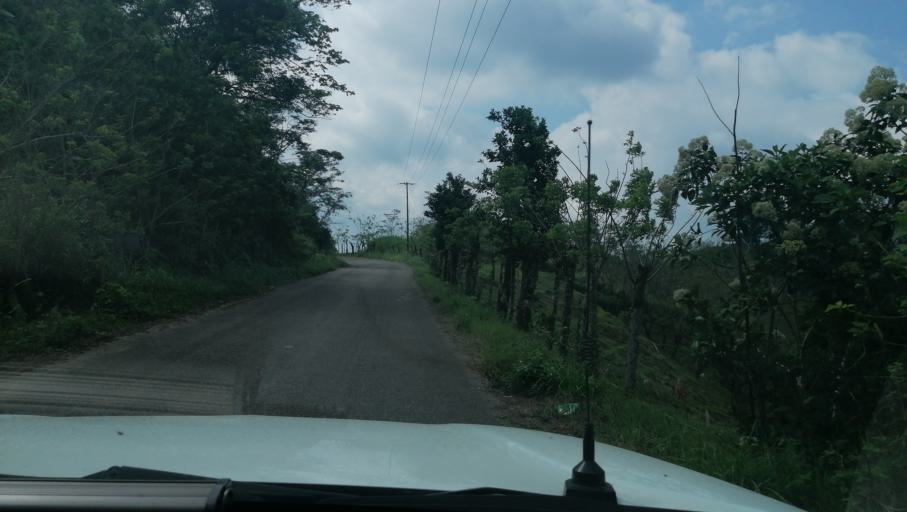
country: MX
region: Chiapas
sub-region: Francisco Leon
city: San Miguel la Sardina
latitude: 17.2390
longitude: -93.3162
